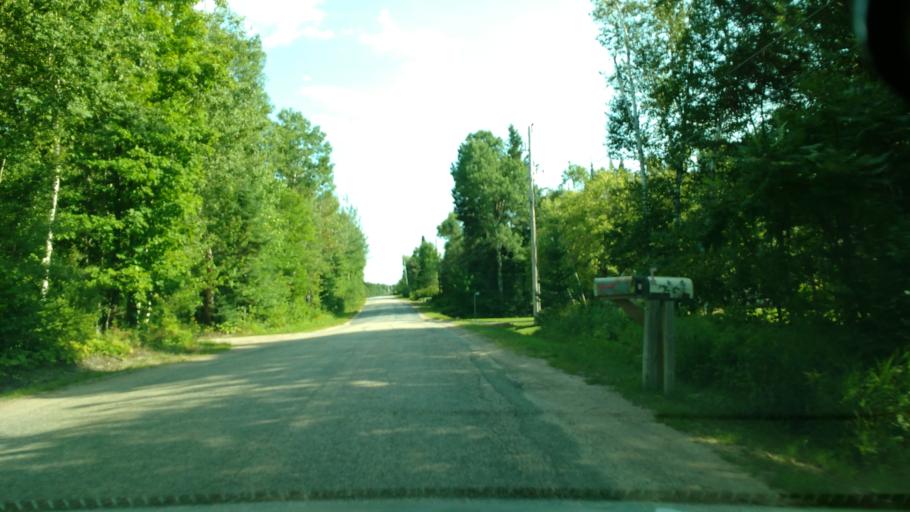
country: CA
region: Ontario
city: Powassan
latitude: 46.1834
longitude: -79.3112
